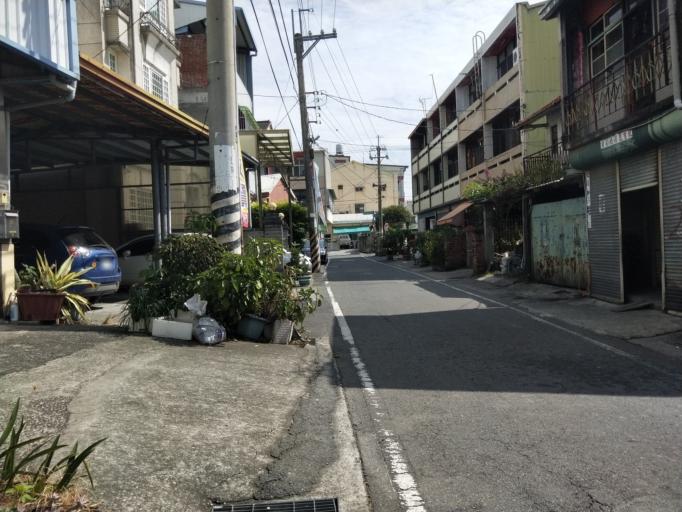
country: TW
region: Taiwan
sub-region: Nantou
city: Nantou
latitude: 23.8502
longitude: 120.5838
